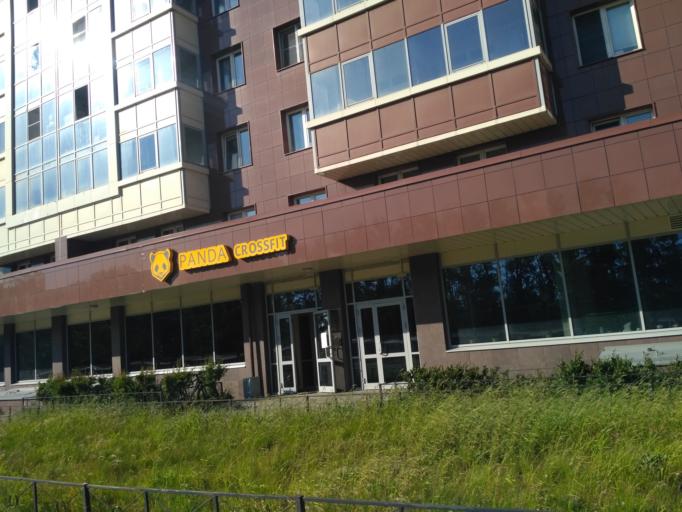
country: RU
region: St.-Petersburg
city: Kushelevka
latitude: 59.9837
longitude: 30.3707
